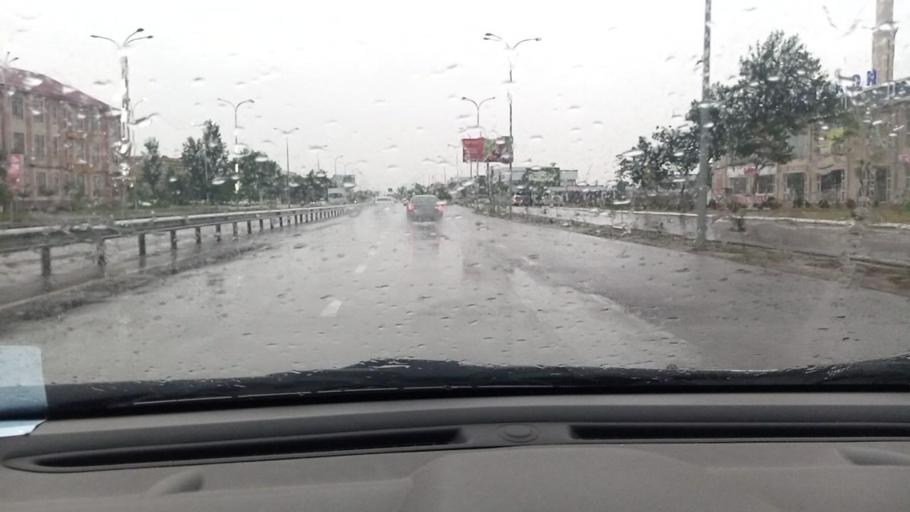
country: UZ
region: Toshkent
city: Ohangaron
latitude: 40.9040
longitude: 69.6399
